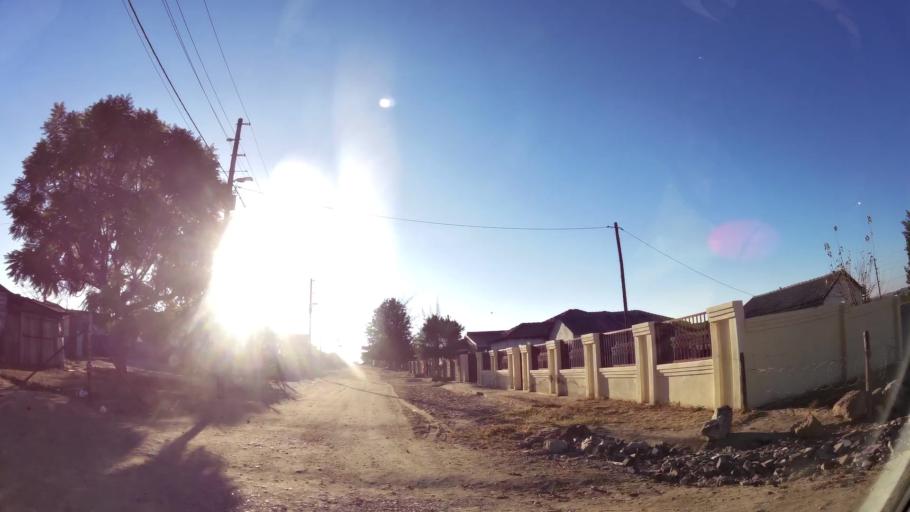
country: ZA
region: Limpopo
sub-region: Capricorn District Municipality
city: Polokwane
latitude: -23.8400
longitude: 29.3596
